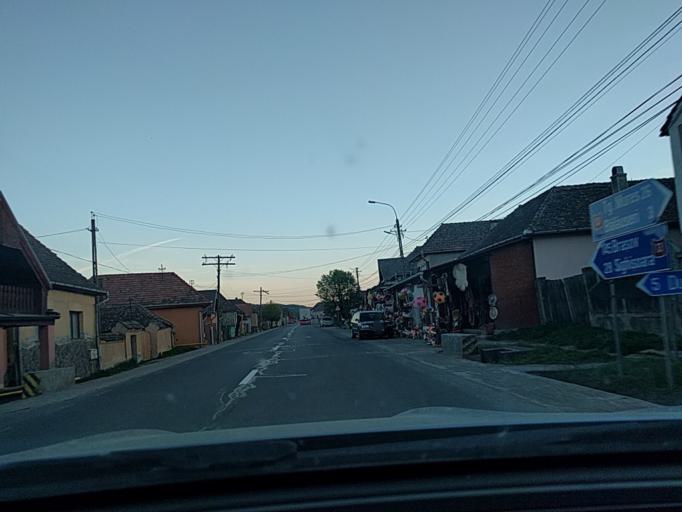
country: RO
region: Mures
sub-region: Comuna Balauseri
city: Chendu
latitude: 46.3887
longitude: 24.7299
